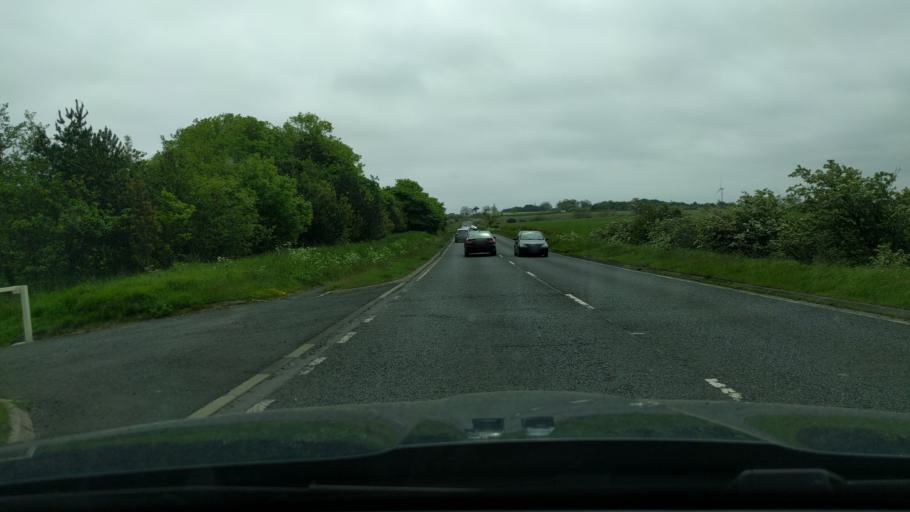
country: GB
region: England
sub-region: Northumberland
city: Cresswell
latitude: 55.2279
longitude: -1.5820
